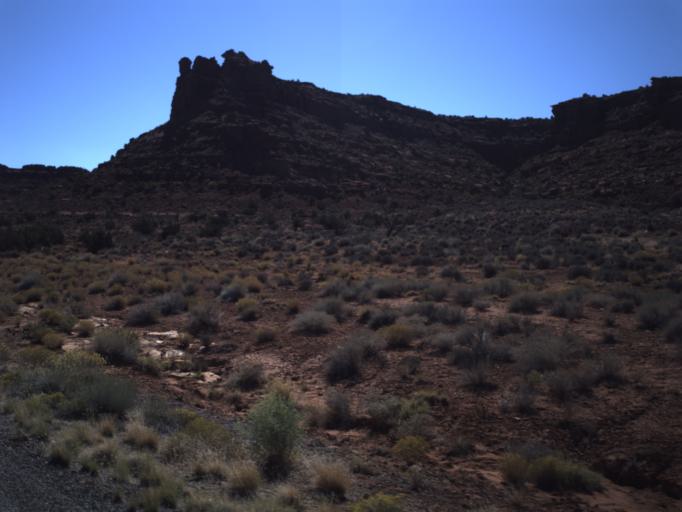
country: US
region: Utah
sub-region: San Juan County
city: Blanding
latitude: 37.8049
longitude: -110.3166
